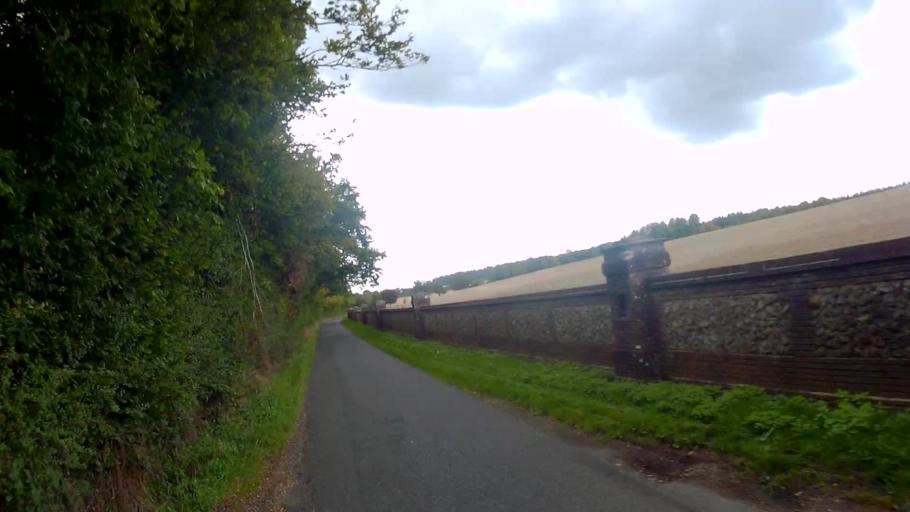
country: GB
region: England
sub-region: Hampshire
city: Overton
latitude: 51.1966
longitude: -1.2819
